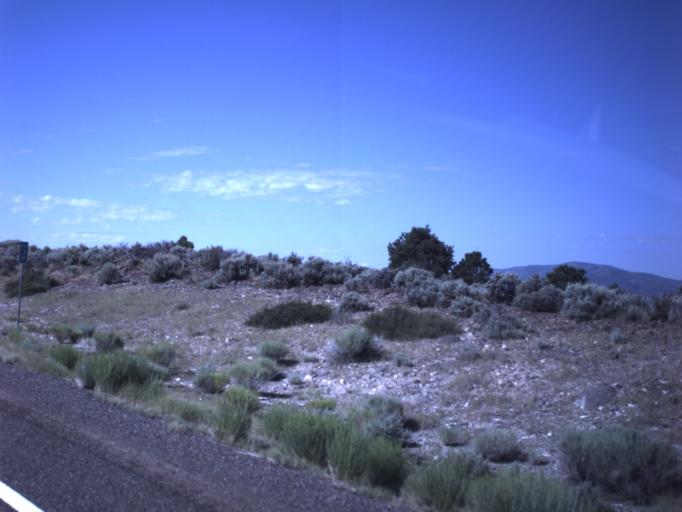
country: US
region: Utah
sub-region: Wayne County
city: Loa
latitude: 38.4739
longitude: -111.8331
